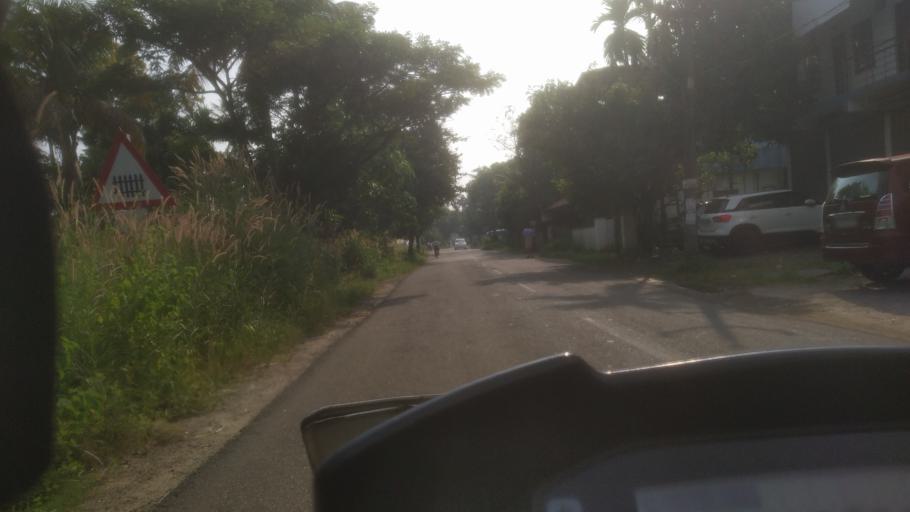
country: IN
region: Kerala
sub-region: Ernakulam
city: Angamali
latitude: 10.1622
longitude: 76.3774
